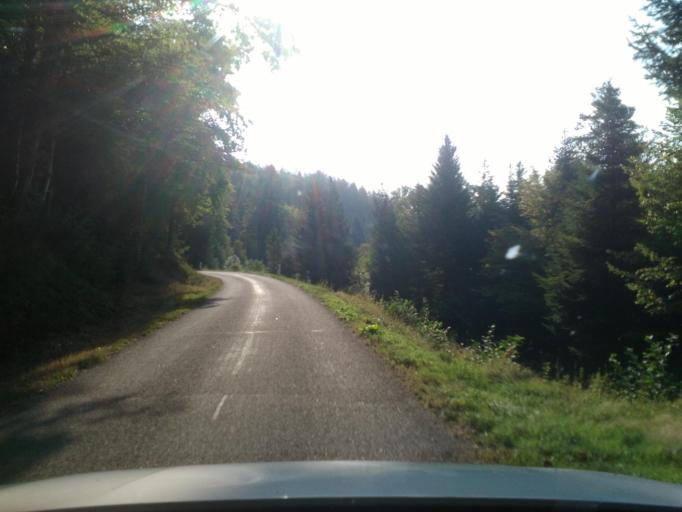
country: FR
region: Lorraine
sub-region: Departement des Vosges
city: Senones
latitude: 48.3865
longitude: 7.0351
